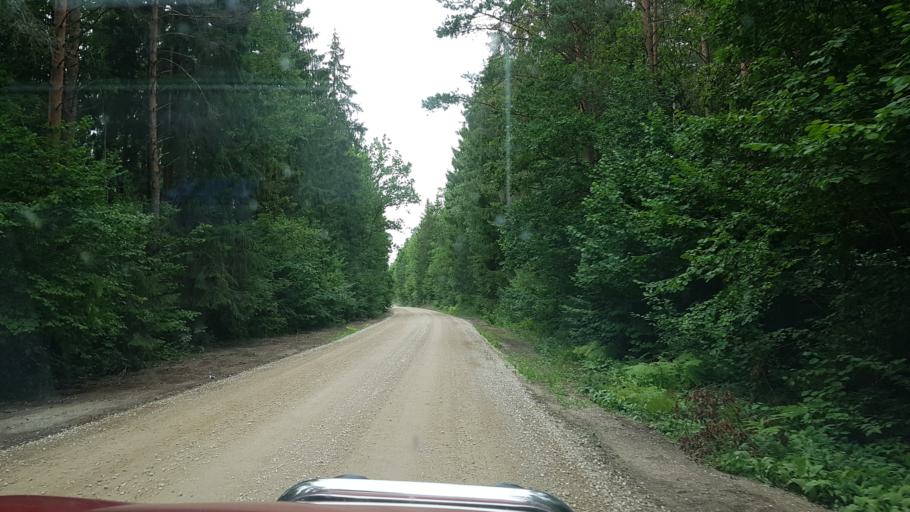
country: EE
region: Laeaene
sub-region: Ridala Parish
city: Uuemoisa
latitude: 58.9811
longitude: 23.8893
